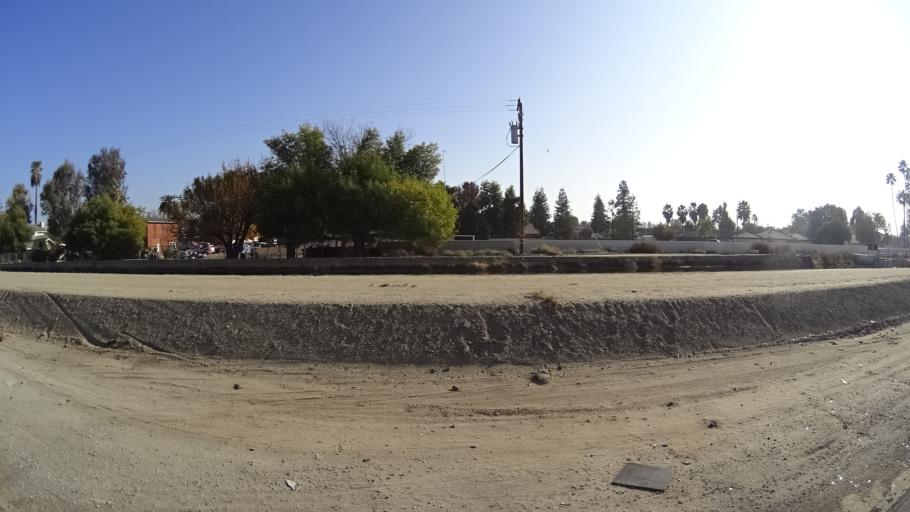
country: US
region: California
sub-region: Kern County
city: Greenfield
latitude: 35.2730
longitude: -119.0213
